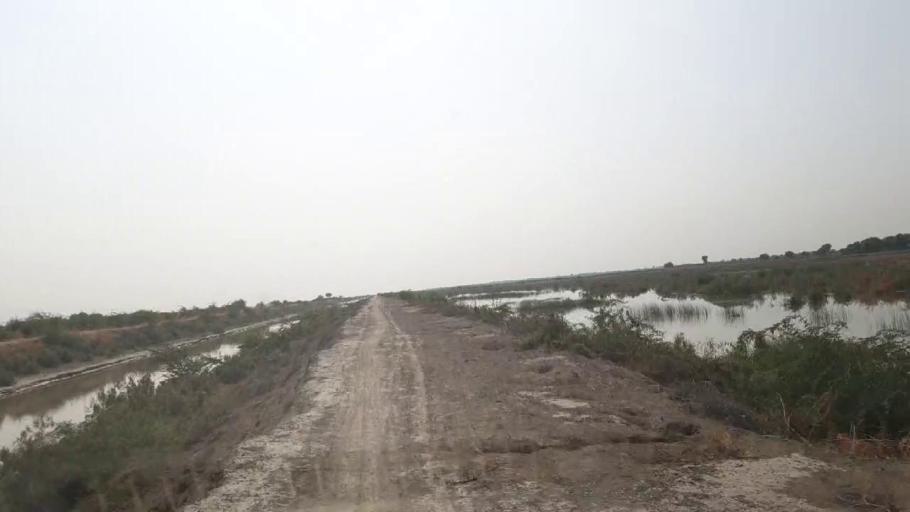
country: PK
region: Sindh
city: Kadhan
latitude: 24.3898
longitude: 68.9019
